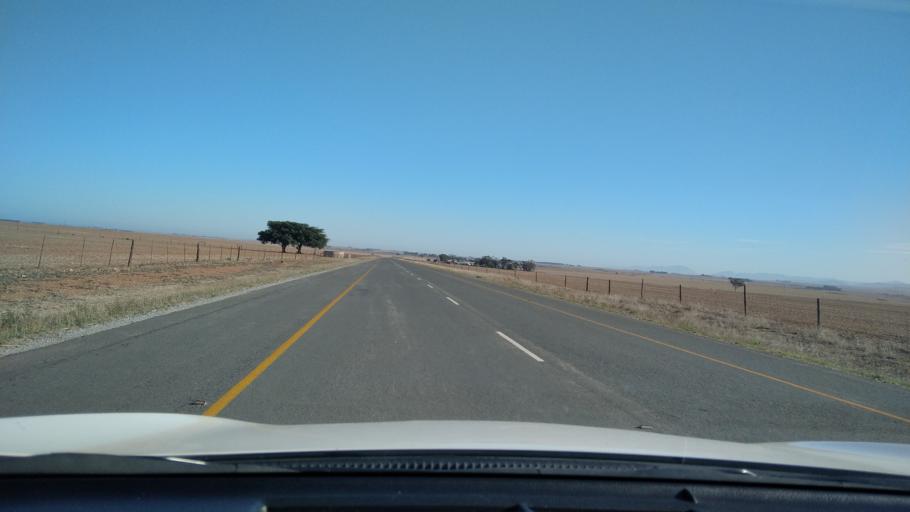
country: ZA
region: Western Cape
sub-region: West Coast District Municipality
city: Moorreesburg
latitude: -33.3140
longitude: 18.6218
